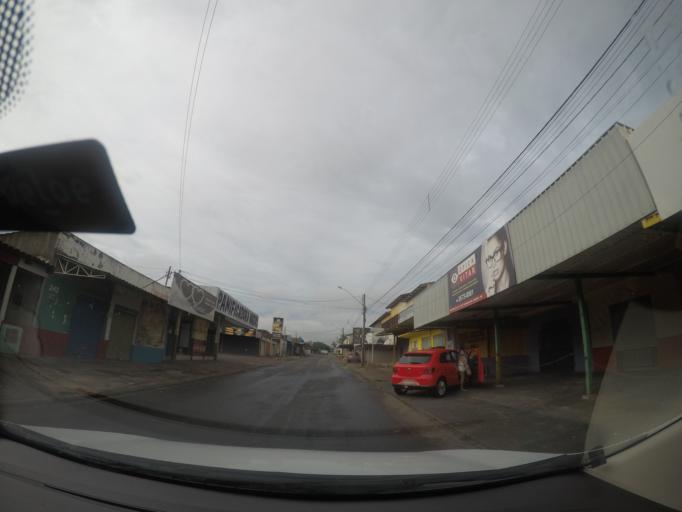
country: BR
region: Goias
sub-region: Goiania
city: Goiania
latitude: -16.6999
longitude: -49.3522
